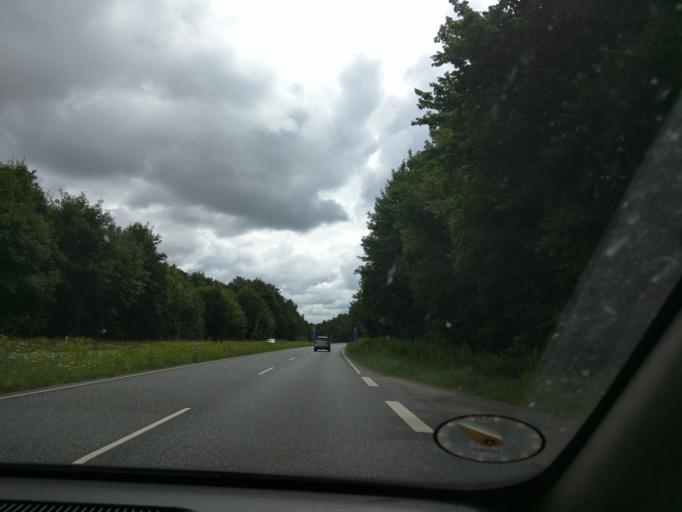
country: DK
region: Zealand
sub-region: Holbaek Kommune
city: Jyderup
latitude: 55.6689
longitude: 11.3639
